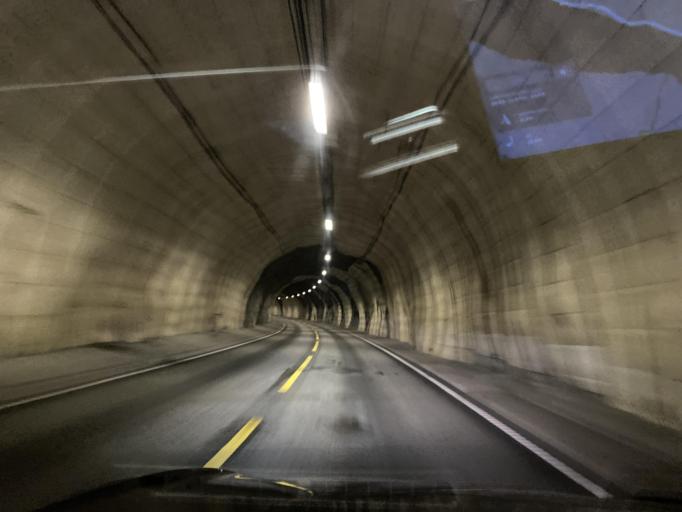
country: NO
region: Rogaland
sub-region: Sauda
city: Sauda
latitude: 59.8418
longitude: 6.3278
